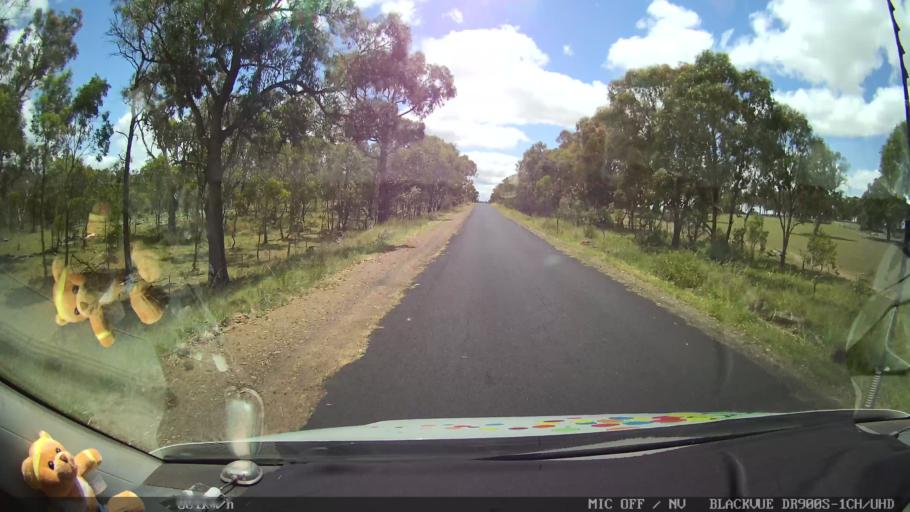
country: AU
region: New South Wales
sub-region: Glen Innes Severn
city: Glen Innes
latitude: -29.4312
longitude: 151.6904
